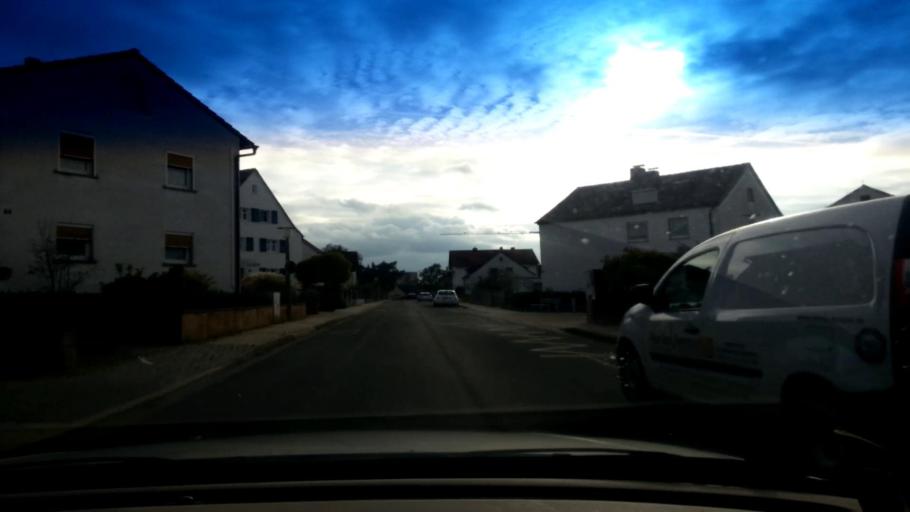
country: DE
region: Bavaria
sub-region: Upper Franconia
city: Hallstadt
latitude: 49.9277
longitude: 10.8838
